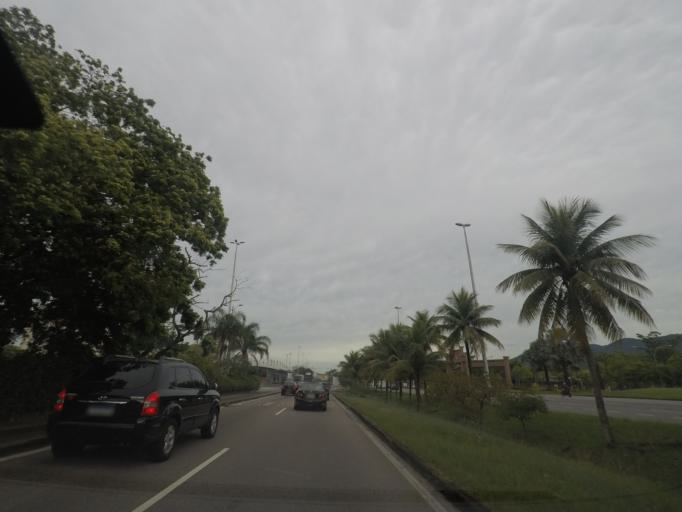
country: BR
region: Rio de Janeiro
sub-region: Nilopolis
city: Nilopolis
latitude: -23.0001
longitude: -43.3974
